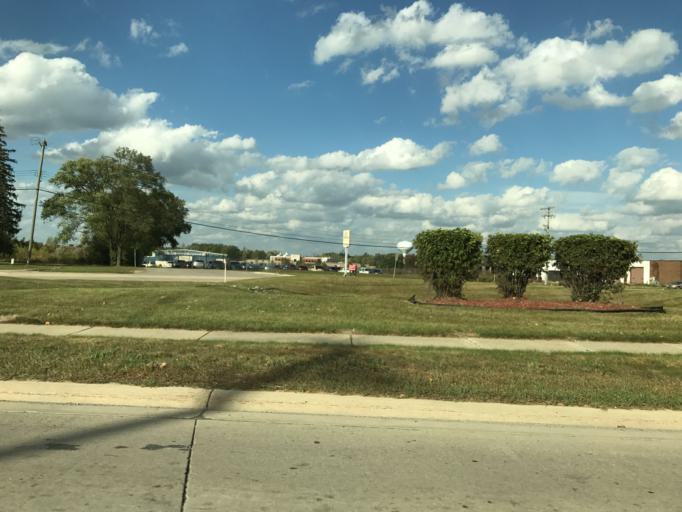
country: US
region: Michigan
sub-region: Oakland County
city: Wixom
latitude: 42.4934
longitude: -83.5317
